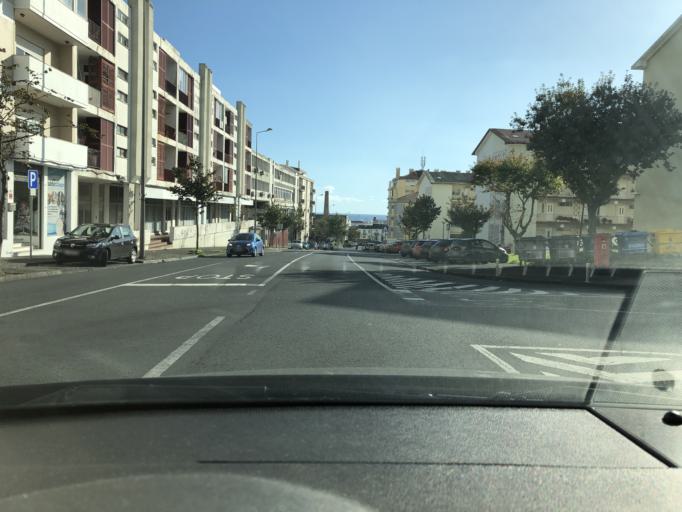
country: PT
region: Azores
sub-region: Ponta Delgada
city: Rosto de Cao
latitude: 37.7452
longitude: -25.6568
